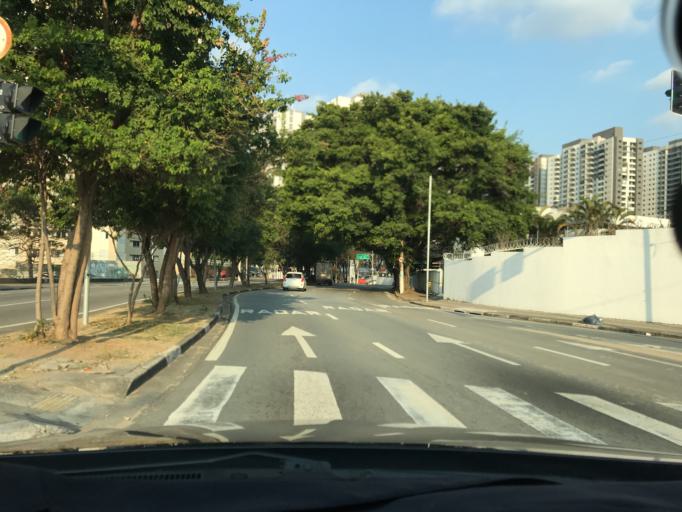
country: BR
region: Sao Paulo
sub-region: Osasco
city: Osasco
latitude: -23.5357
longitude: -46.7651
